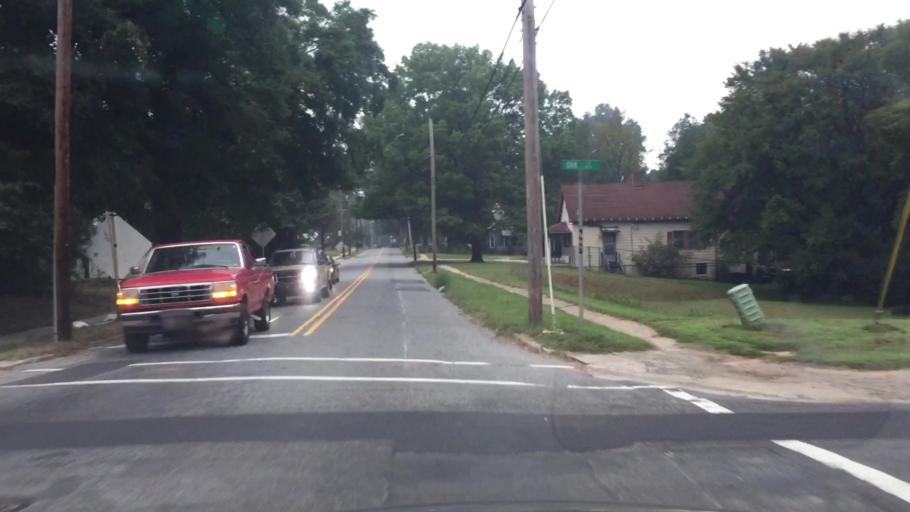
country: US
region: North Carolina
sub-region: Iredell County
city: Mooresville
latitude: 35.5890
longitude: -80.8044
